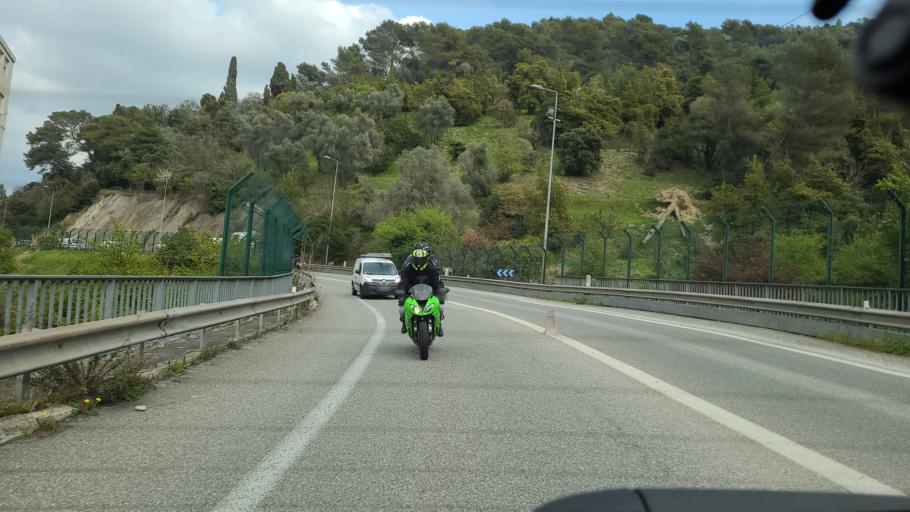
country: FR
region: Provence-Alpes-Cote d'Azur
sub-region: Departement des Alpes-Maritimes
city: Saint-Andre-de-la-Roche
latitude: 43.7309
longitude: 7.2907
